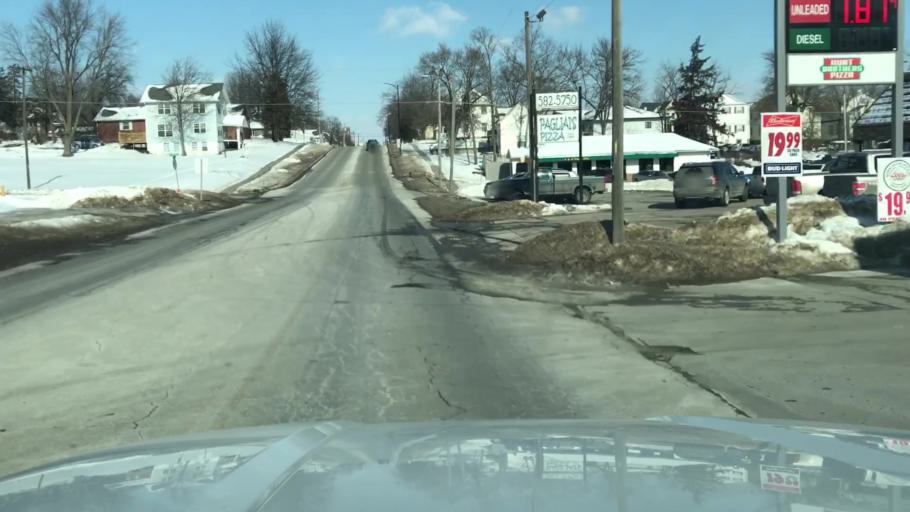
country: US
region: Missouri
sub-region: Nodaway County
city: Maryville
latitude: 40.3407
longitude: -94.8730
